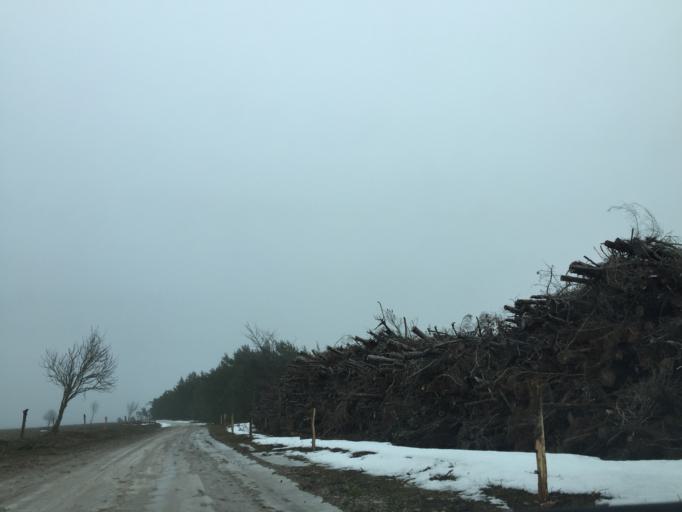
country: EE
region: Saare
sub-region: Kuressaare linn
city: Kuressaare
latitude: 58.5115
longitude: 21.9395
